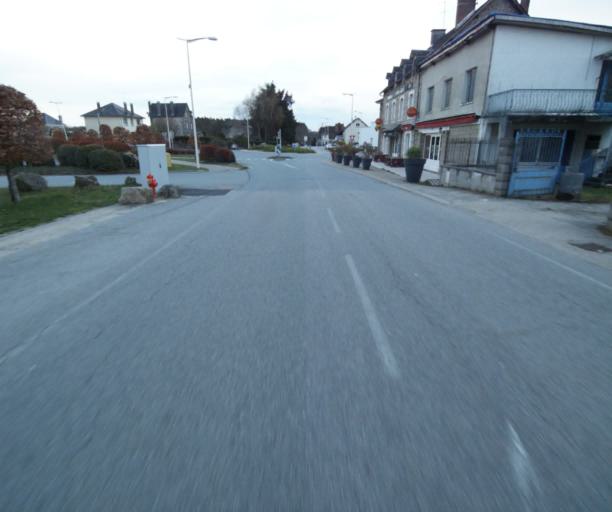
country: FR
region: Limousin
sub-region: Departement de la Correze
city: Correze
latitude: 45.3325
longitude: 1.8791
